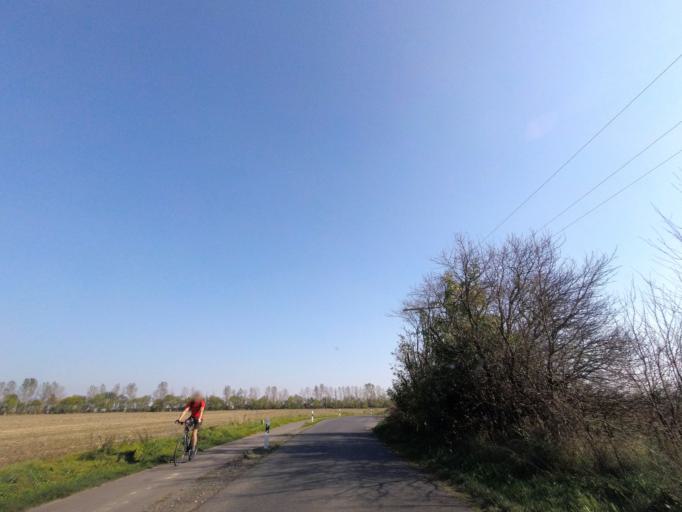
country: DE
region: Brandenburg
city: Niedergorsdorf
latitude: 51.9510
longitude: 12.9892
